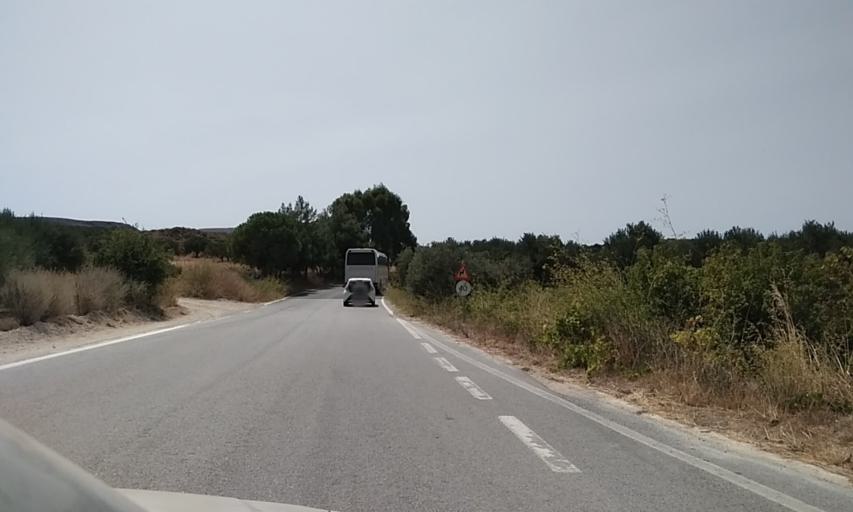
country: GR
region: Crete
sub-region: Nomos Lasithiou
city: Makry-Gialos
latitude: 35.1013
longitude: 26.0601
